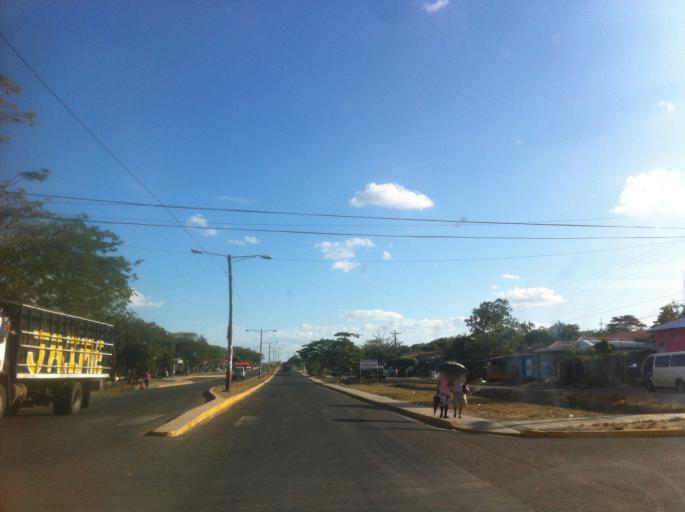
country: NI
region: Chontales
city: Acoyapa
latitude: 11.9691
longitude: -85.1674
